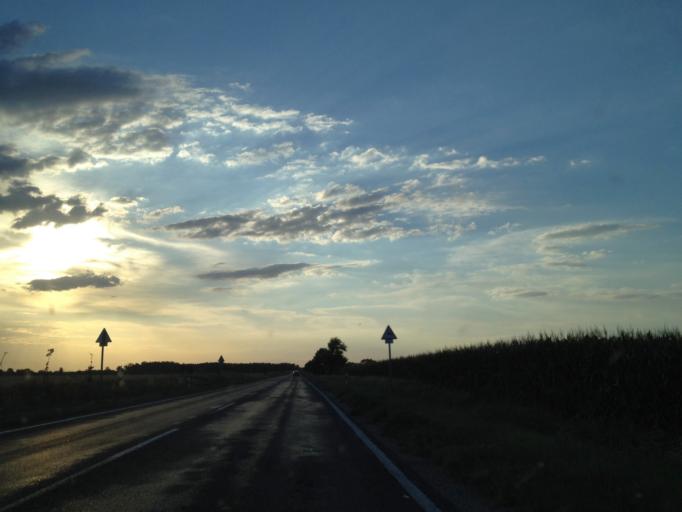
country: HU
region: Gyor-Moson-Sopron
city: Otteveny
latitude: 47.7455
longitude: 17.4607
